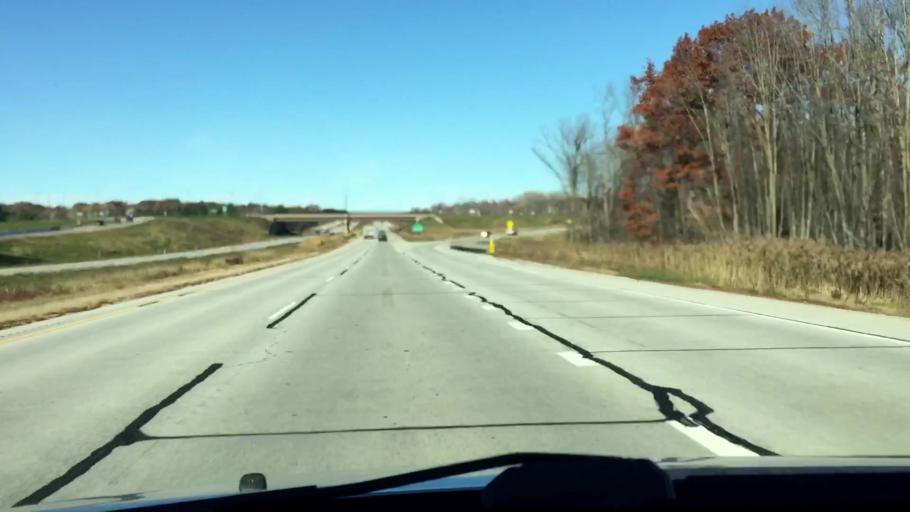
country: US
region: Wisconsin
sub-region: Brown County
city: Howard
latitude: 44.5588
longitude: -88.1259
